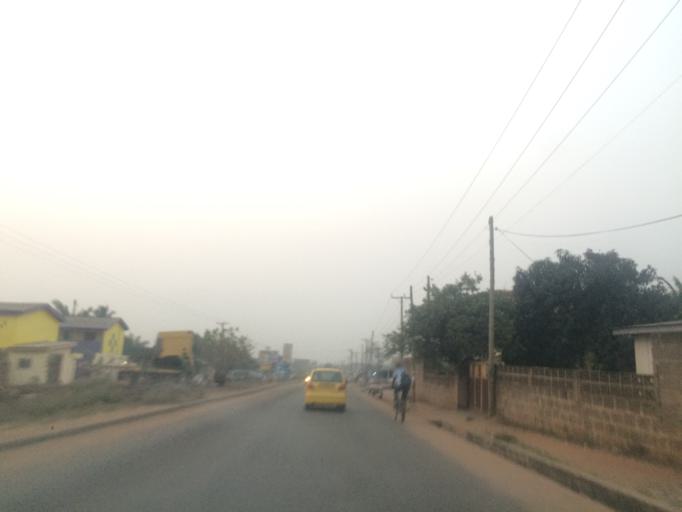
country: GH
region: Greater Accra
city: Teshi Old Town
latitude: 5.5937
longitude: -0.1007
